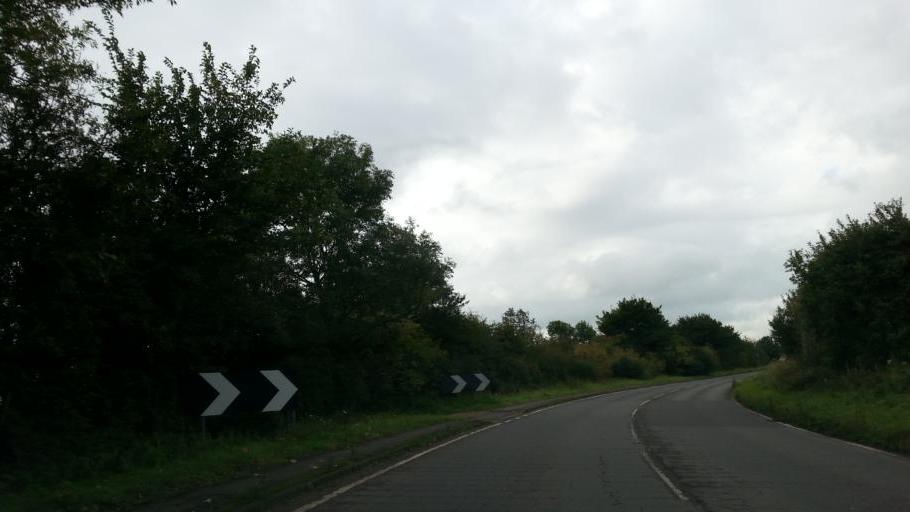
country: GB
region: England
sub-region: Hertfordshire
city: Hitchin
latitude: 51.9761
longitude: -0.2891
